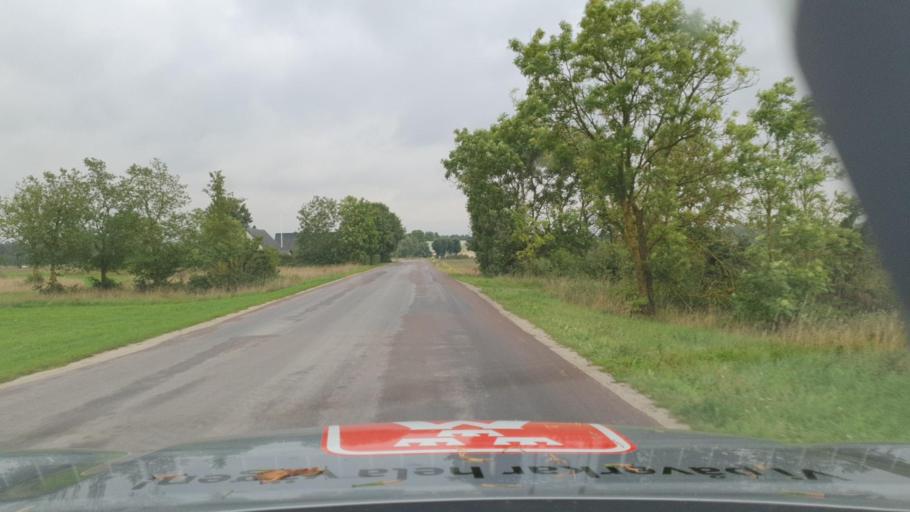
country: SE
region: Gotland
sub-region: Gotland
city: Visby
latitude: 57.6463
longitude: 18.5520
